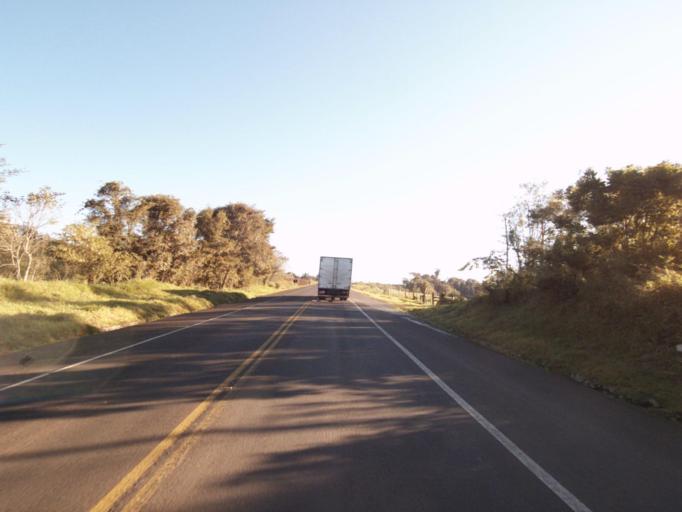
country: BR
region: Santa Catarina
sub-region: Chapeco
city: Chapeco
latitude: -26.9017
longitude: -52.8911
